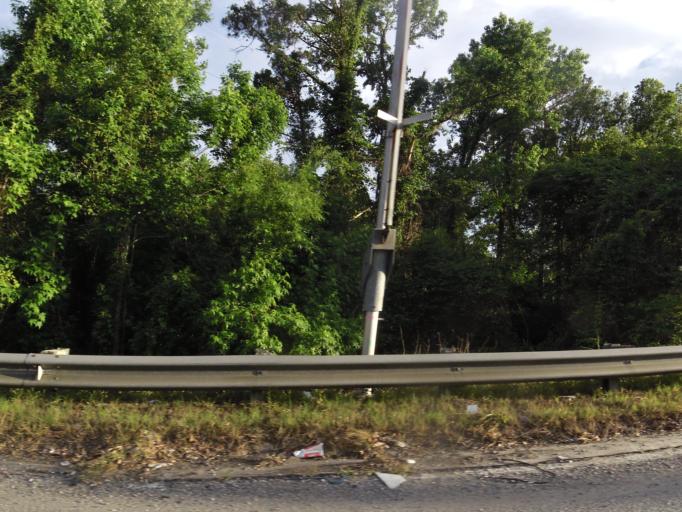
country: US
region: Georgia
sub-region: Chatham County
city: Pooler
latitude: 32.0696
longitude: -81.2030
